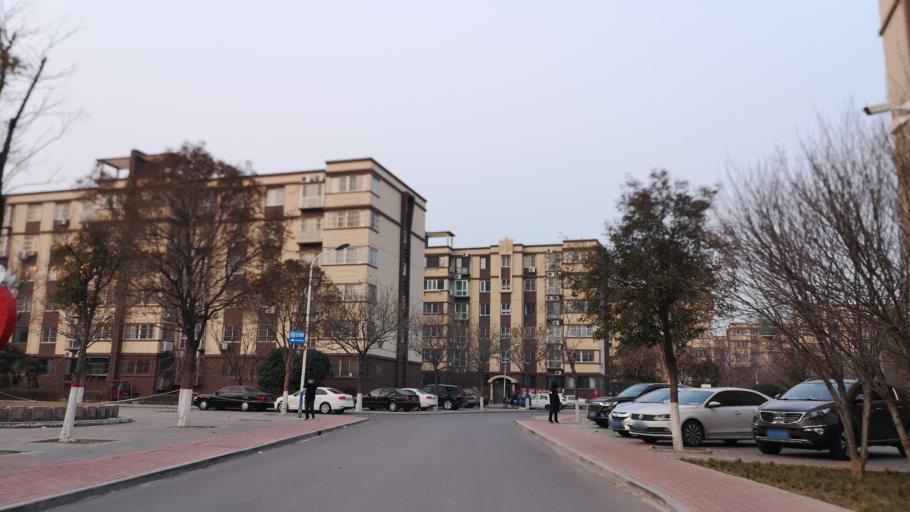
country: CN
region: Henan Sheng
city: Zhongyuanlu
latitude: 35.7871
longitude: 115.0782
